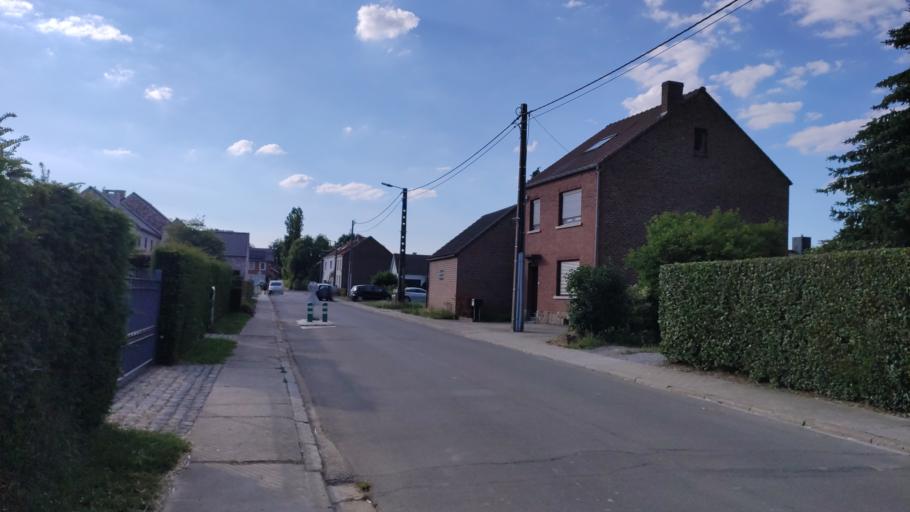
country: BE
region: Flanders
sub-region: Provincie Vlaams-Brabant
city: Hoegaarden
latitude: 50.7600
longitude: 4.8816
